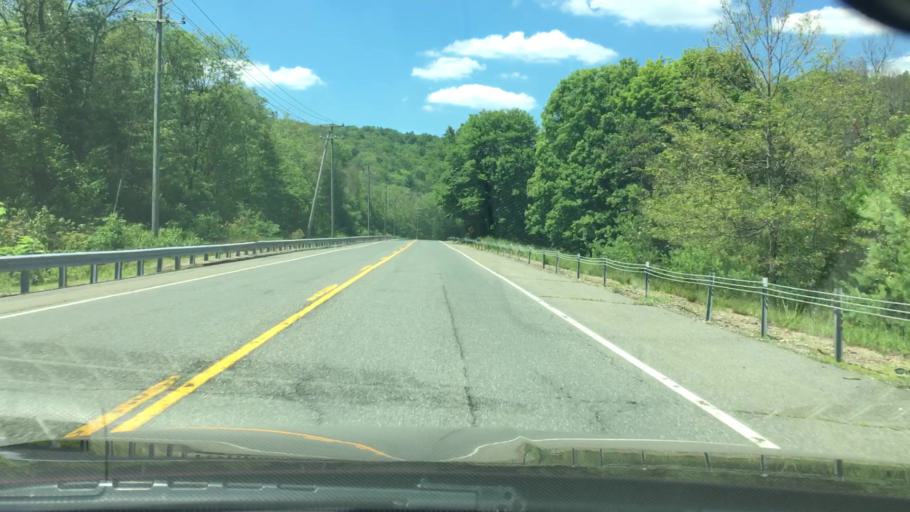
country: US
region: Connecticut
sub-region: Tolland County
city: Stafford Springs
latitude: 41.9103
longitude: -72.2938
